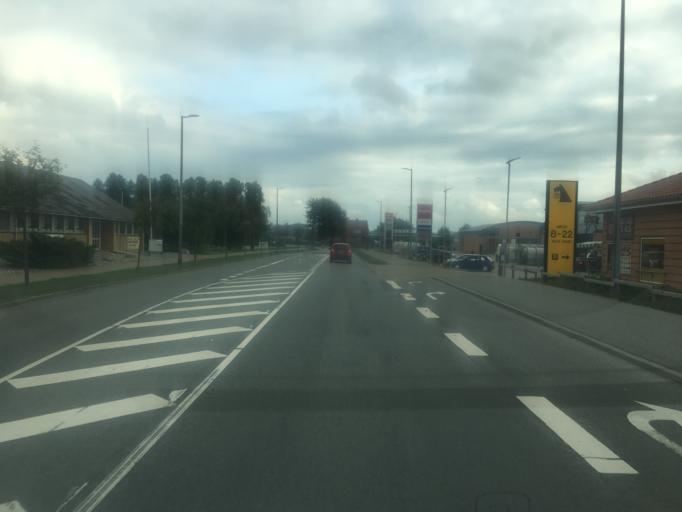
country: DK
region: South Denmark
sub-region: Tonder Kommune
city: Tonder
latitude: 54.9402
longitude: 8.8557
